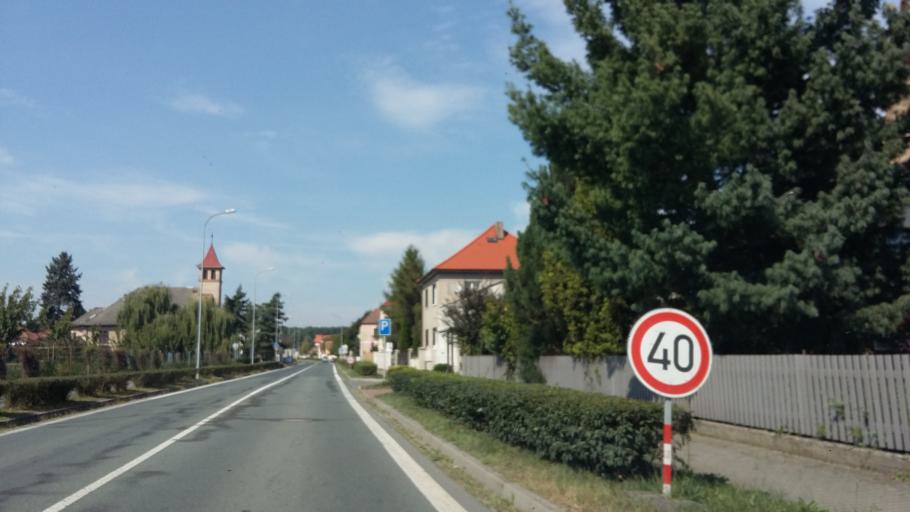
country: CZ
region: Central Bohemia
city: Velky Osek
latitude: 50.0946
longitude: 15.1863
